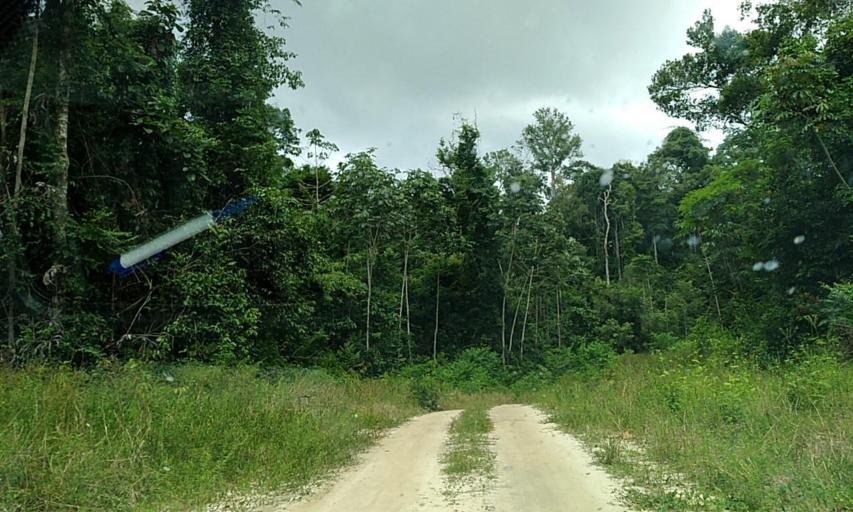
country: BR
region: Para
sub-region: Altamira
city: Altamira
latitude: -3.0607
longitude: -52.9088
